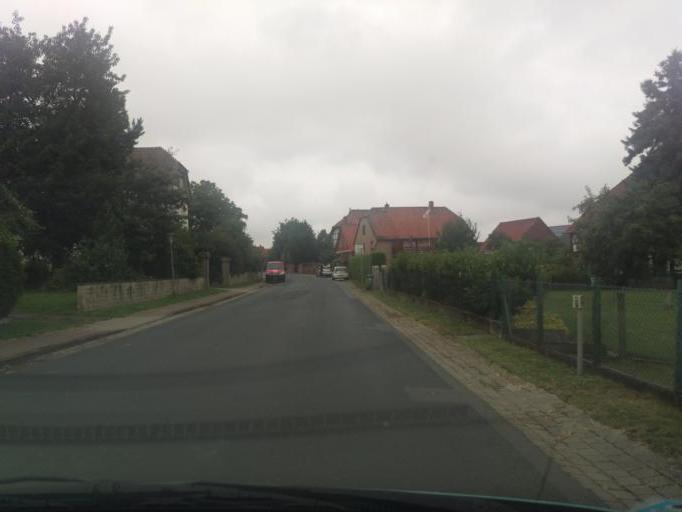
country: DE
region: Lower Saxony
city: Hohenhameln
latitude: 52.2427
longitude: 10.1178
